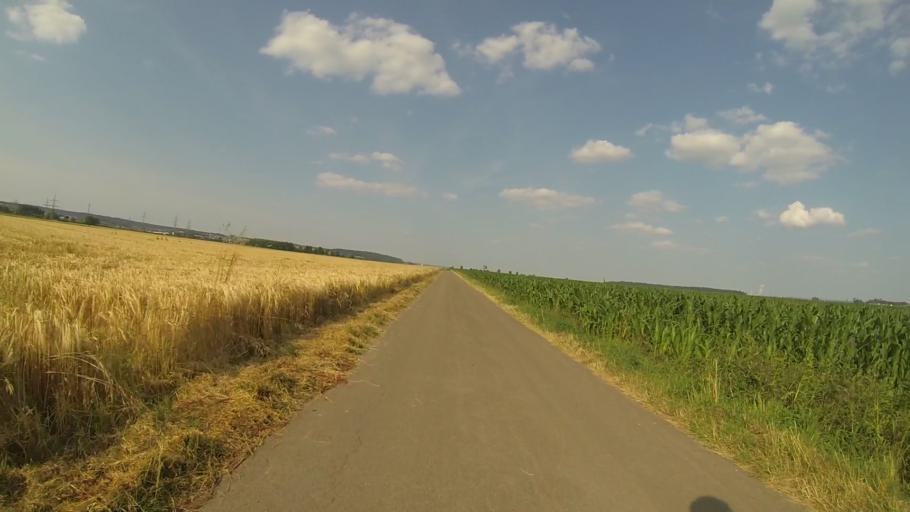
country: DE
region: Baden-Wuerttemberg
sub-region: Regierungsbezirk Stuttgart
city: Niederstotzingen
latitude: 48.5177
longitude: 10.2312
